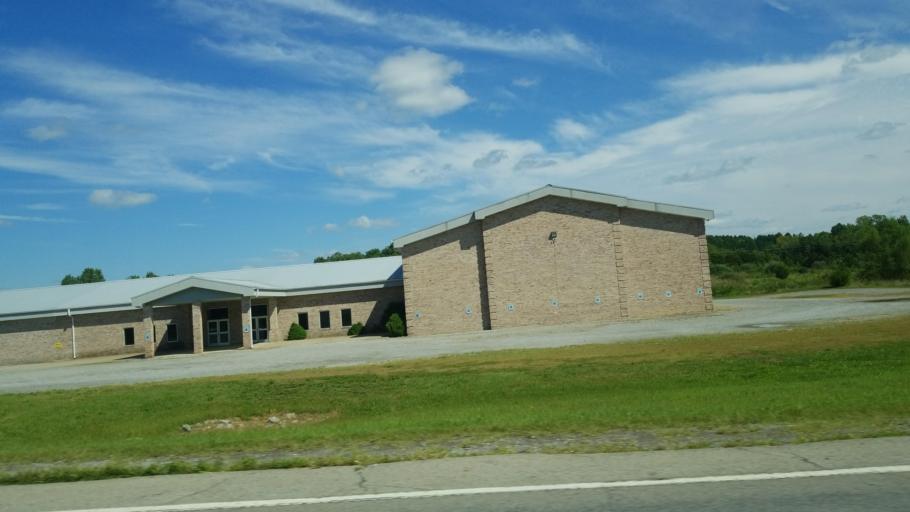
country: US
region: Illinois
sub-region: Williamson County
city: Marion
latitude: 37.7625
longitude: -88.9328
